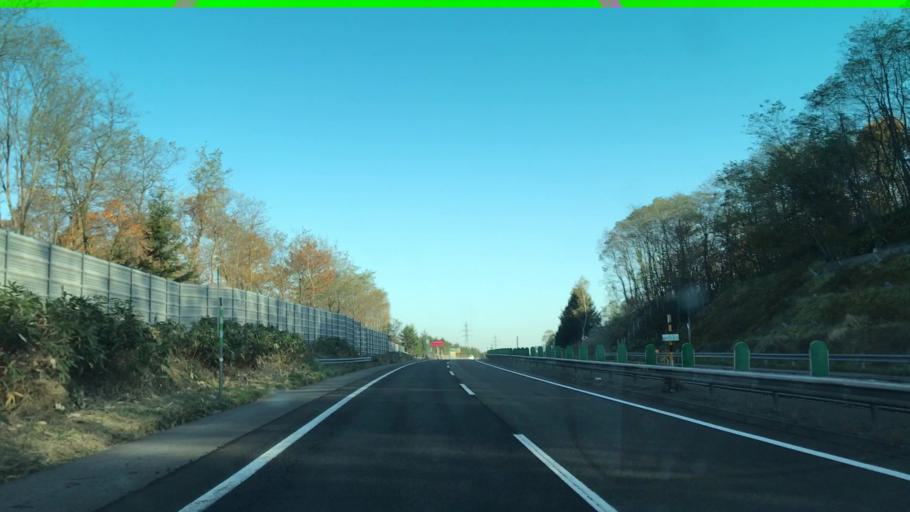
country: JP
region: Hokkaido
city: Sunagawa
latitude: 43.4216
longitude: 141.9111
